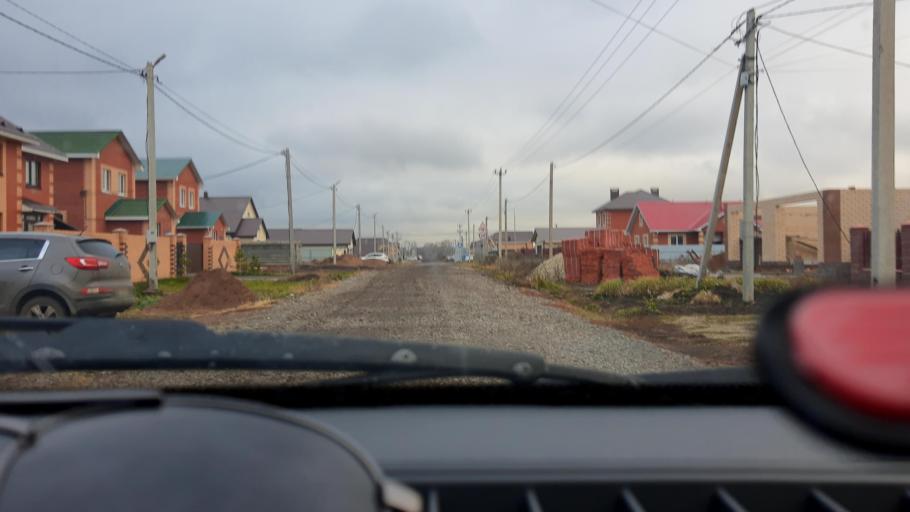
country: RU
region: Bashkortostan
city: Ufa
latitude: 54.6087
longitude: 55.9137
